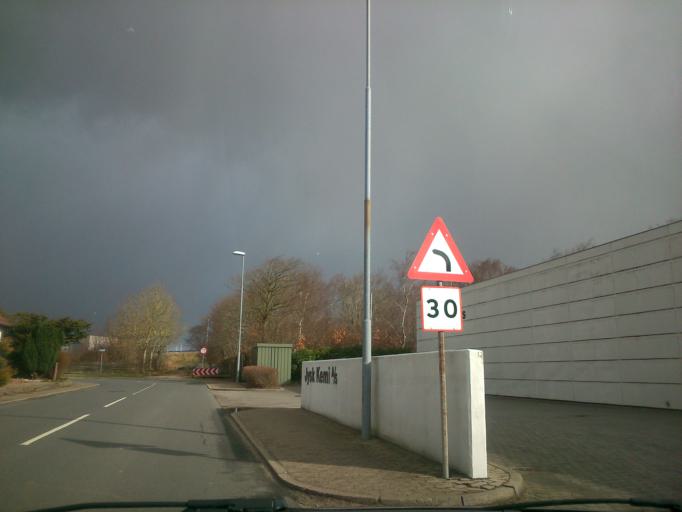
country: DK
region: Central Jutland
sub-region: Holstebro Kommune
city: Holstebro
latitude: 56.3738
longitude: 8.6204
